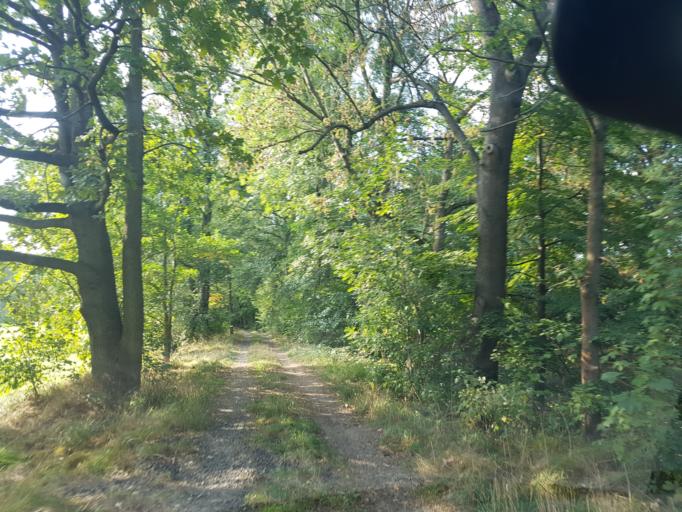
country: DE
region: Saxony
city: Waldheim
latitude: 51.0803
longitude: 13.0207
